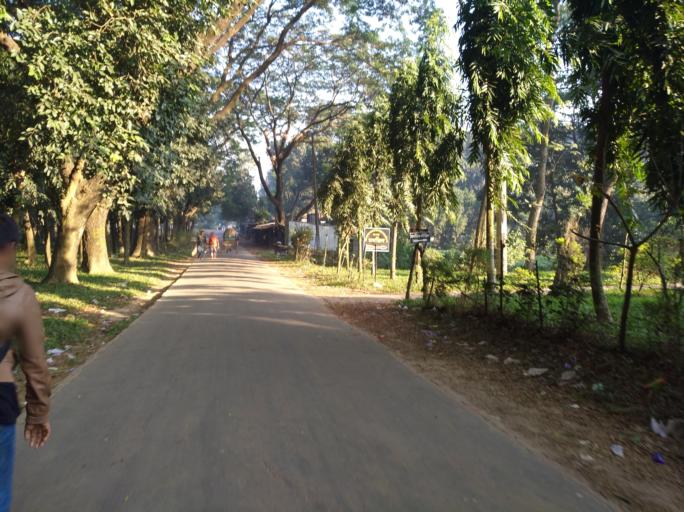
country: BD
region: Dhaka
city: Tungi
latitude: 23.8821
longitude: 90.2652
